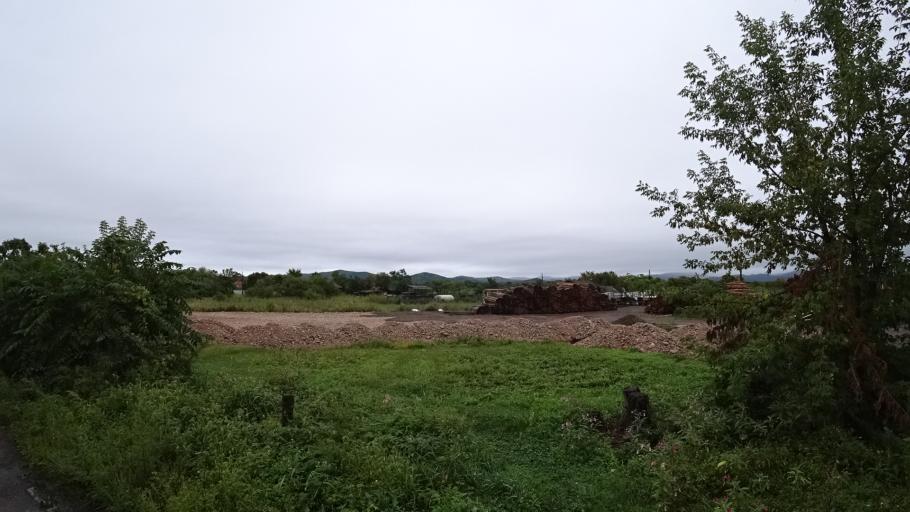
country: RU
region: Primorskiy
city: Monastyrishche
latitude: 44.2117
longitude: 132.4480
